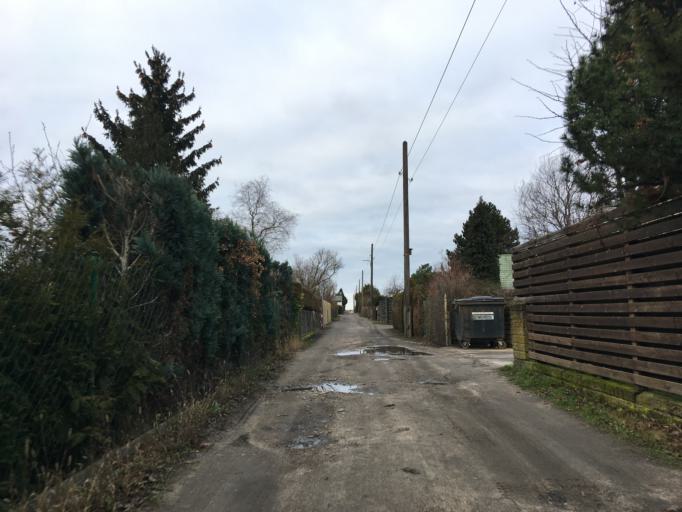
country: DE
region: Berlin
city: Buchholz
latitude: 52.6023
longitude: 13.4129
